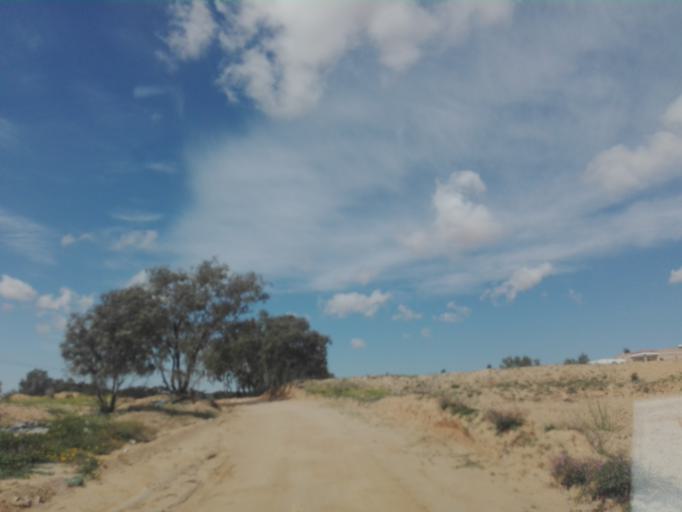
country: TN
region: Safaqis
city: Sfax
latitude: 34.7294
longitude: 10.5014
